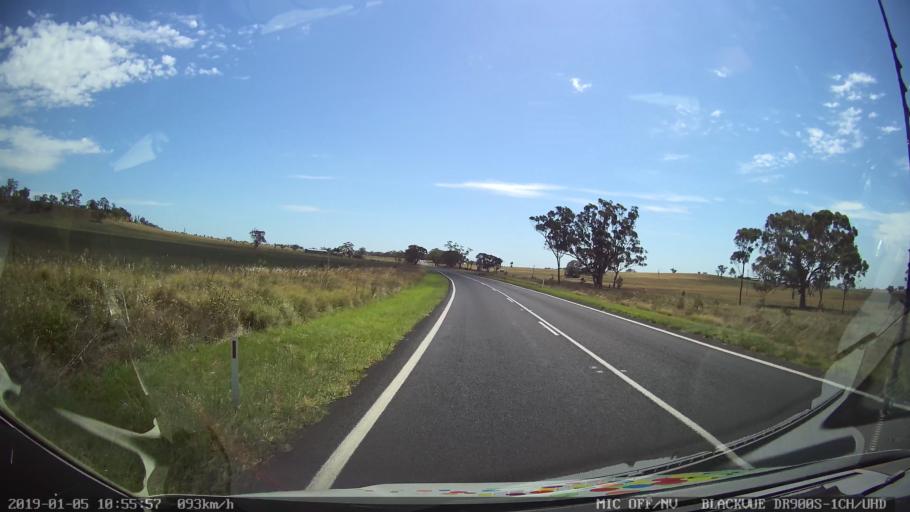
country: AU
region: New South Wales
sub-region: Warrumbungle Shire
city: Coonabarabran
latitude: -31.4458
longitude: 149.1513
